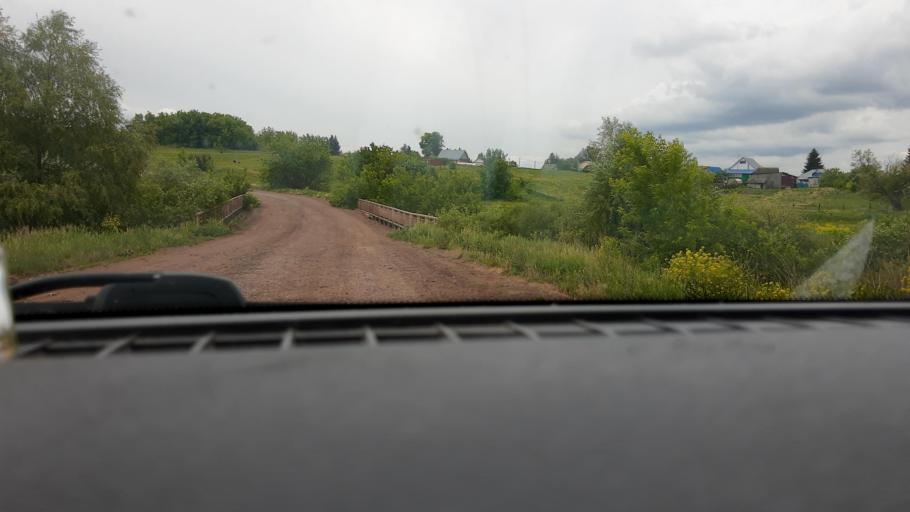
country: RU
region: Bashkortostan
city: Chishmy
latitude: 54.6825
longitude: 55.4822
